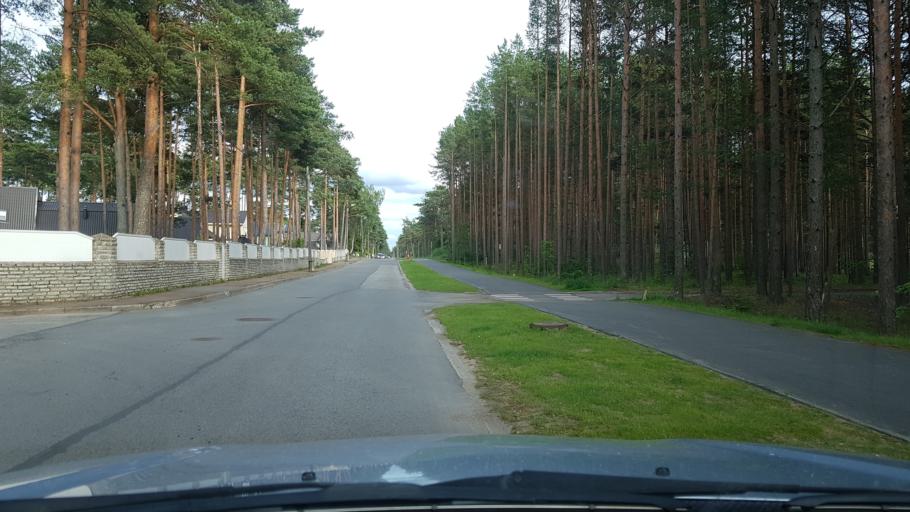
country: EE
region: Ida-Virumaa
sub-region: Narva-Joesuu linn
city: Narva-Joesuu
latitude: 59.4557
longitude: 28.0446
